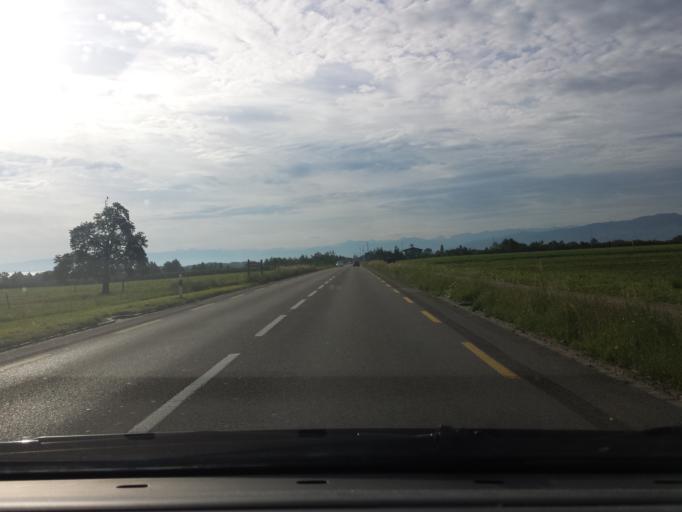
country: CH
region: Thurgau
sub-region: Arbon District
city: Egnach
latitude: 47.5244
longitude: 9.3921
